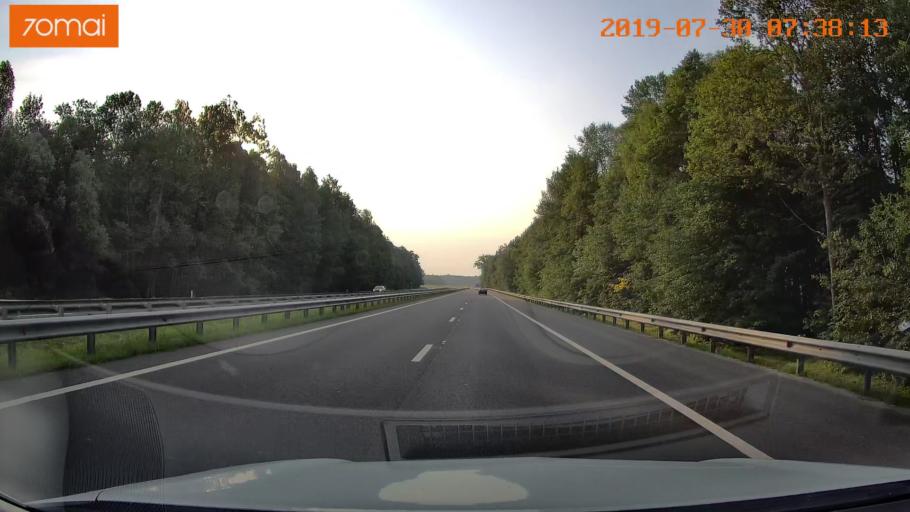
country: RU
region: Kaliningrad
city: Gvardeysk
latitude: 54.6509
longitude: 21.1627
